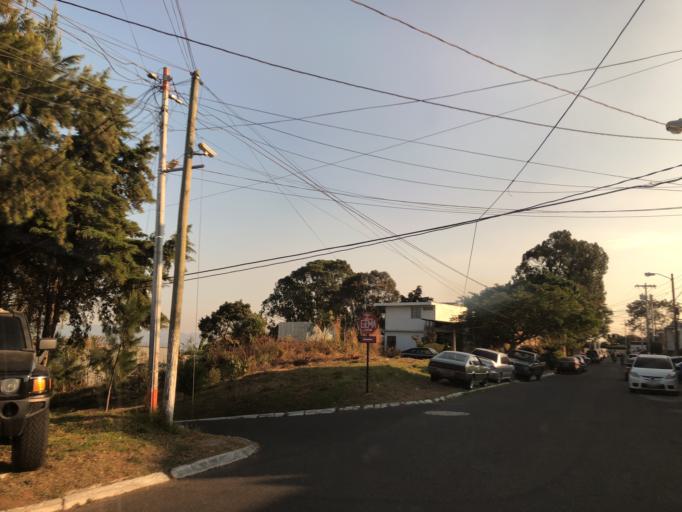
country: GT
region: Guatemala
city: Mixco
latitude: 14.6280
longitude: -90.5943
